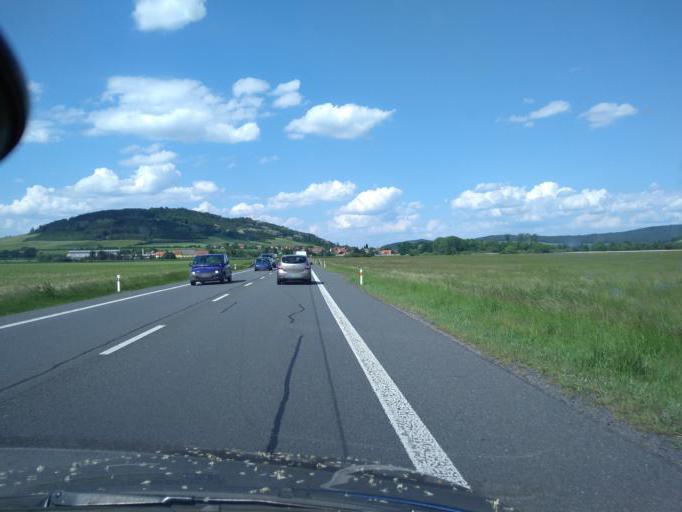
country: CZ
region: Plzensky
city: Svihov
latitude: 49.4946
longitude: 13.2893
